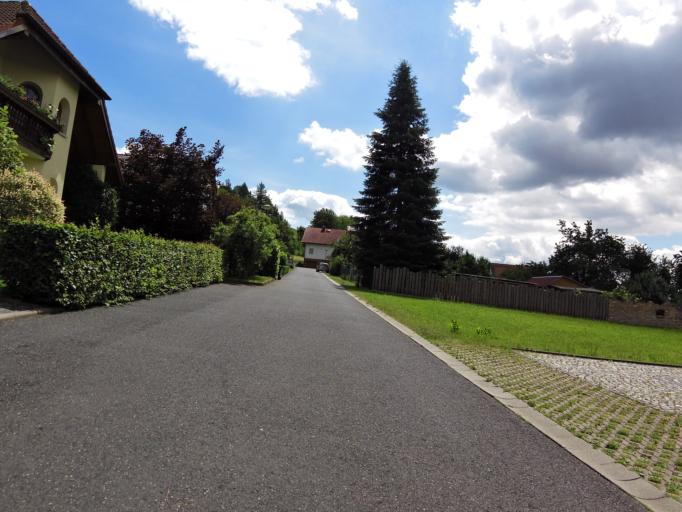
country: DE
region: Thuringia
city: Lauchroden
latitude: 50.9942
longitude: 10.1617
